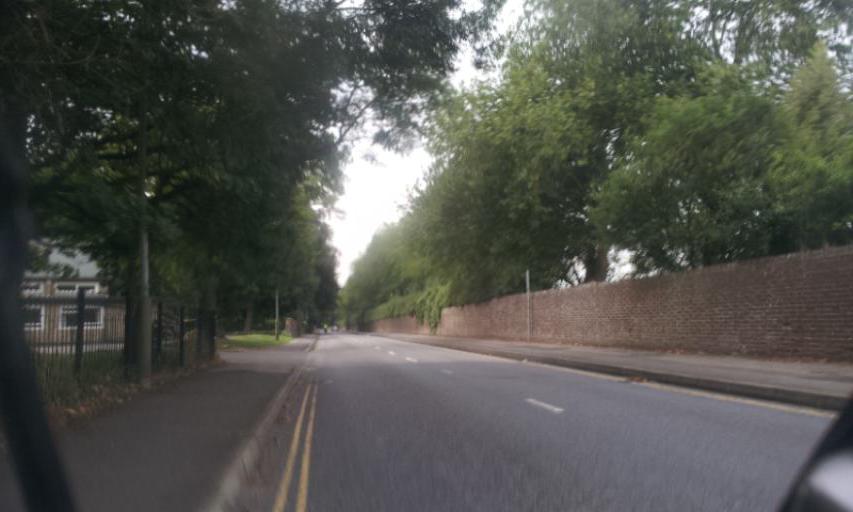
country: GB
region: England
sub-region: Kent
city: Larkfield
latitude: 51.2892
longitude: 0.4388
